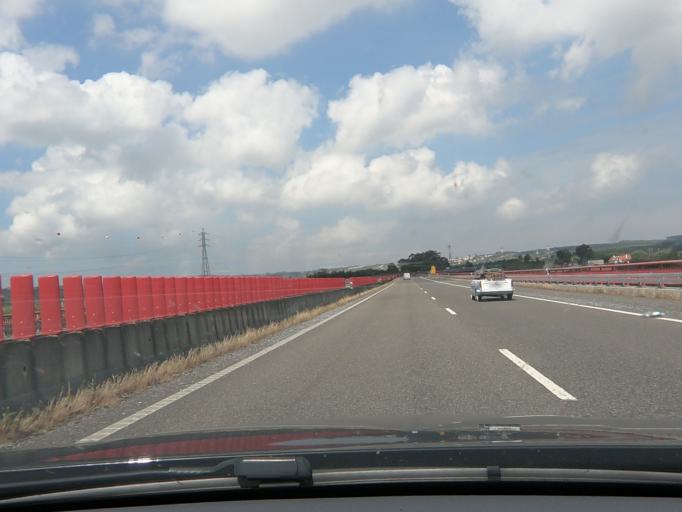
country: PT
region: Leiria
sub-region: Obidos
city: Obidos
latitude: 39.3338
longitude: -9.1990
